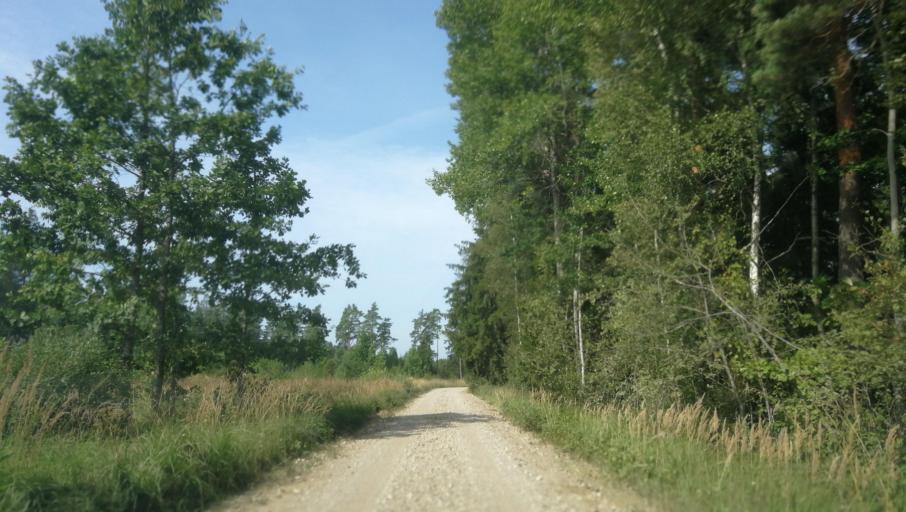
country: LV
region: Pavilostas
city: Pavilosta
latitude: 56.8340
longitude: 21.2817
